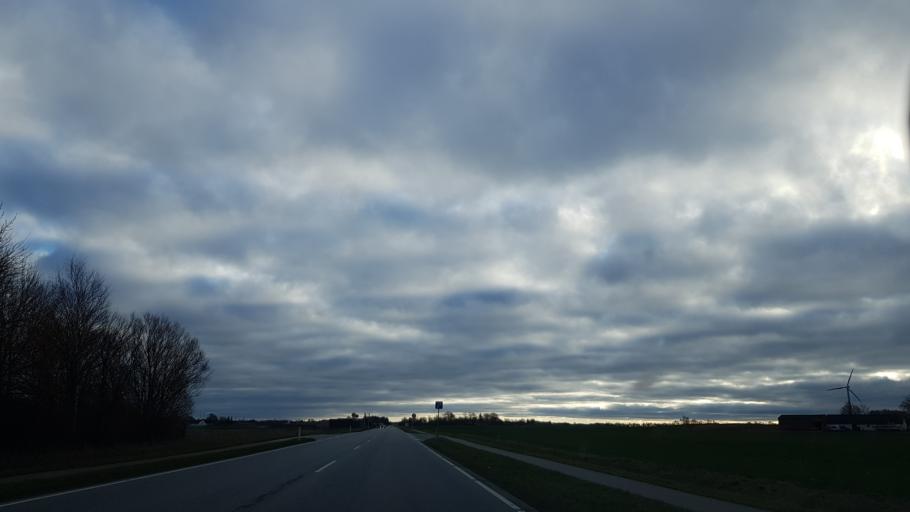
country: DK
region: Zealand
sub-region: Kalundborg Kommune
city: Gorlev
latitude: 55.5313
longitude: 11.2282
